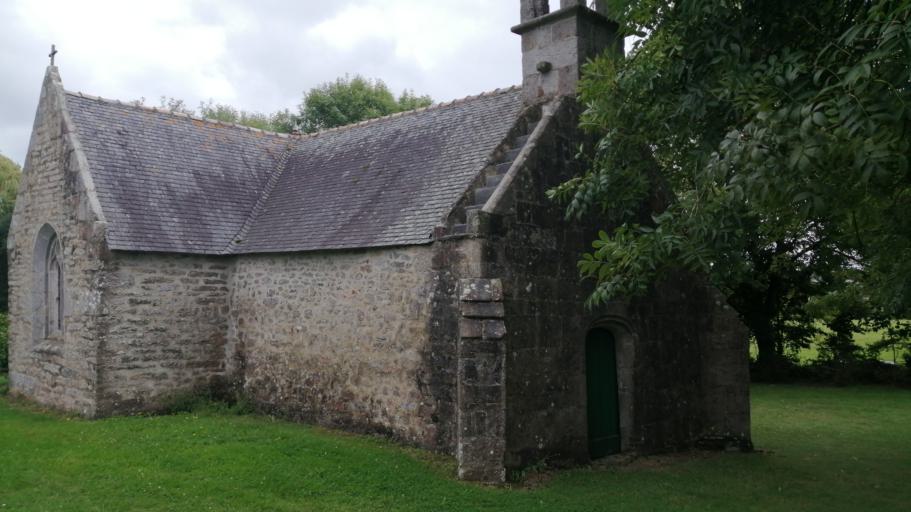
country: FR
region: Brittany
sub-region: Departement du Finistere
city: Poullan-sur-Mer
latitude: 48.0869
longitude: -4.4610
